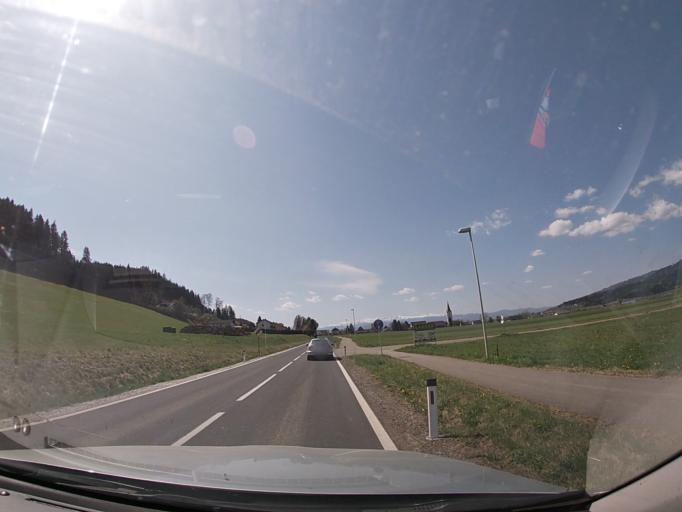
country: AT
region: Styria
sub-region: Politischer Bezirk Murtal
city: Sankt Margarethen bei Knittelfeld
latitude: 47.2311
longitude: 14.8637
